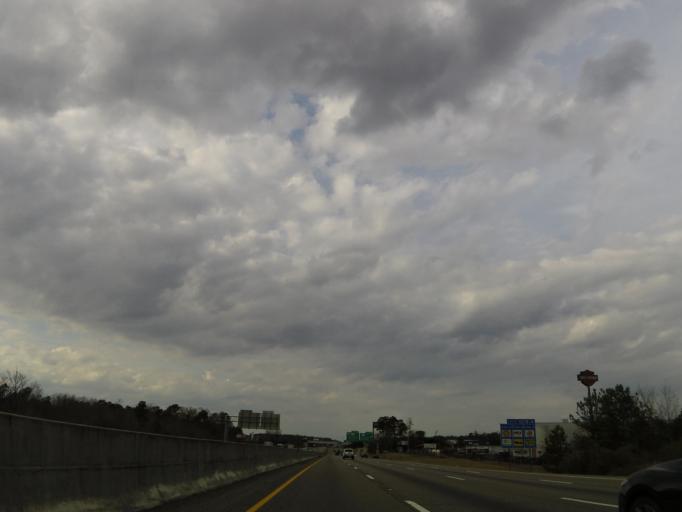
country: US
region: South Carolina
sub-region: Lexington County
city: Irmo
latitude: 34.0936
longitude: -81.1689
